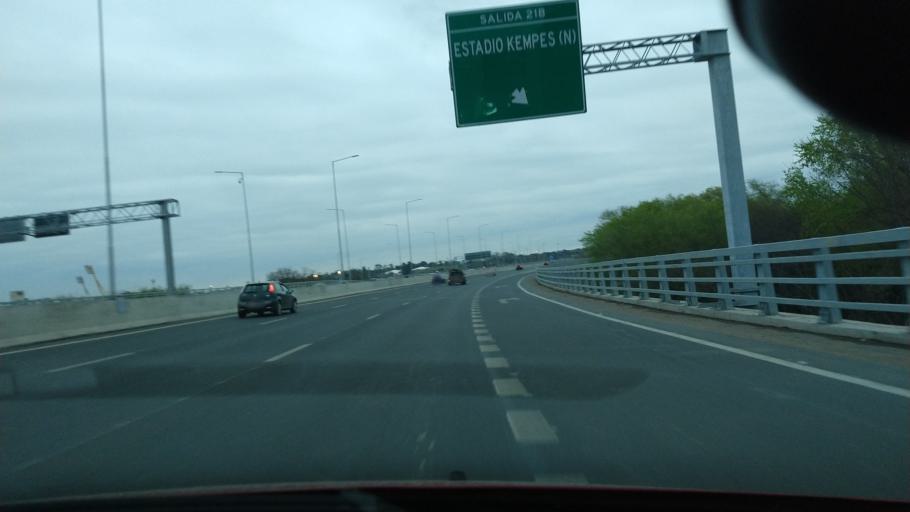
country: AR
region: Cordoba
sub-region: Departamento de Capital
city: Cordoba
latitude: -31.3622
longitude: -64.2432
